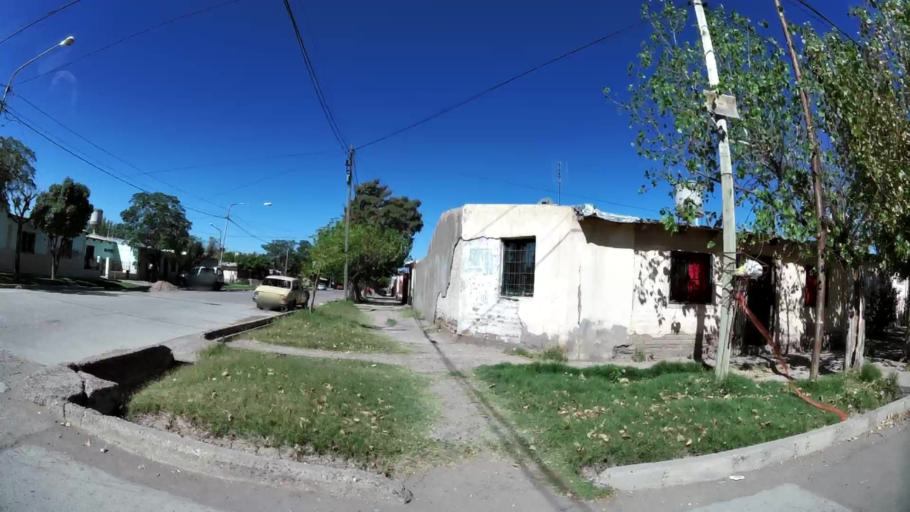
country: AR
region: Mendoza
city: Las Heras
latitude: -32.8260
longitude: -68.8155
